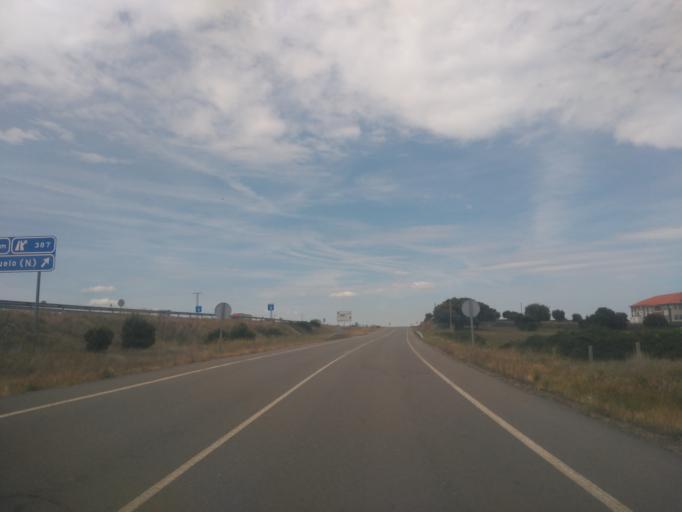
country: ES
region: Castille and Leon
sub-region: Provincia de Salamanca
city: Guijuelo
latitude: 40.5630
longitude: -5.6603
